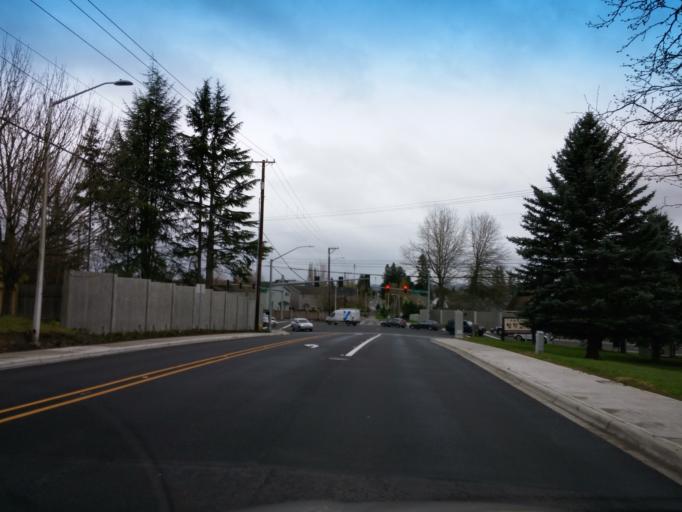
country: US
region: Oregon
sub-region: Washington County
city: Oak Hills
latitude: 45.5234
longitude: -122.8548
